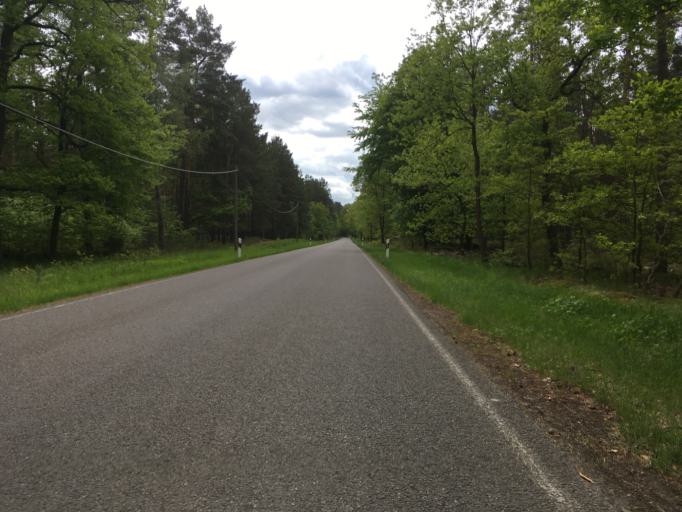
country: DE
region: Brandenburg
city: Joachimsthal
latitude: 52.9937
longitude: 13.7416
